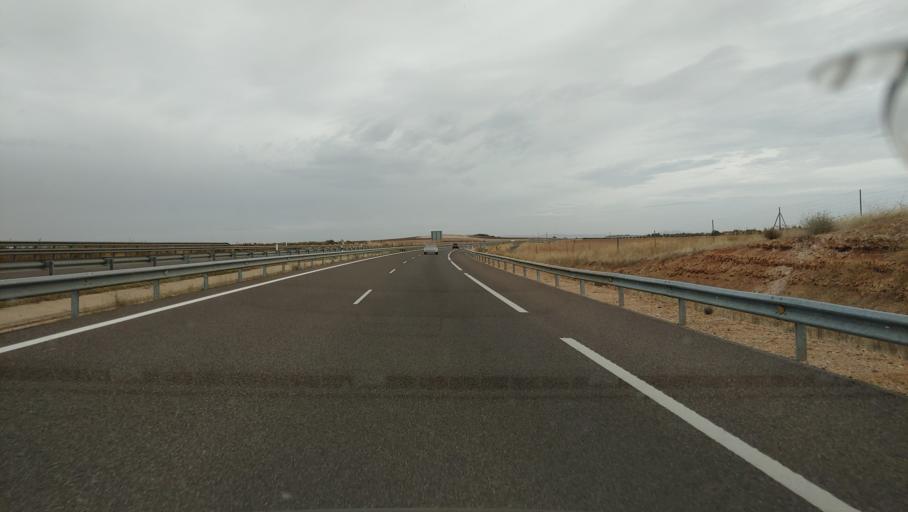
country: ES
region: Castille-La Mancha
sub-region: Provincia de Ciudad Real
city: Miguelturra
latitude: 38.9129
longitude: -3.8561
